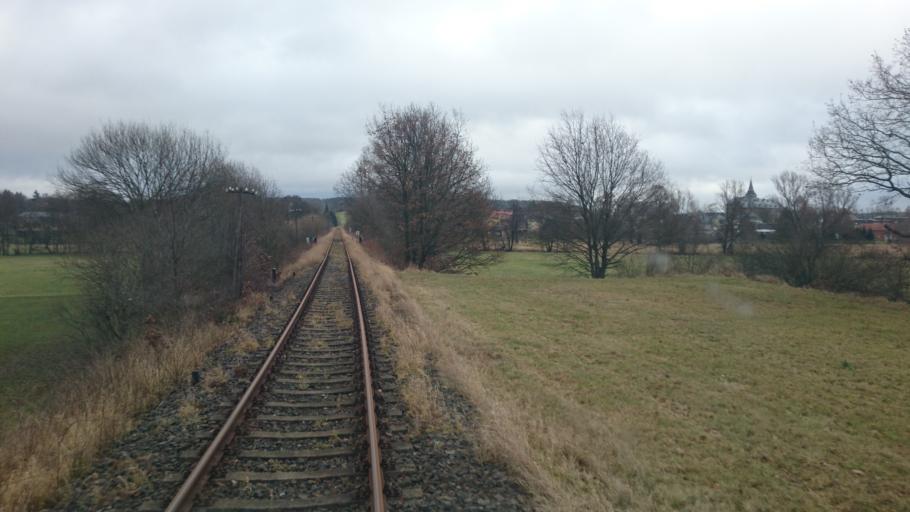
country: DE
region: Saxony
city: Muhltroff
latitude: 50.5433
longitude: 11.9235
